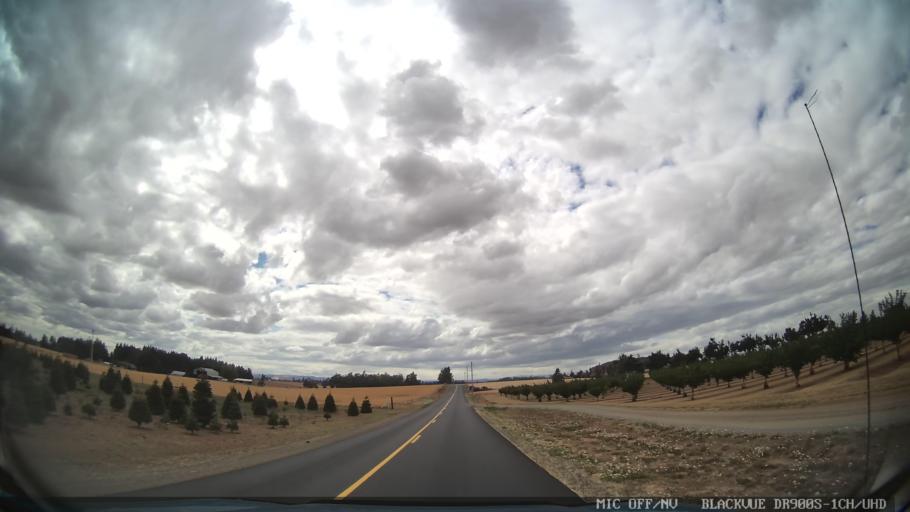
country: US
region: Oregon
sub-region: Marion County
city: Sublimity
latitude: 44.8405
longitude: -122.7888
